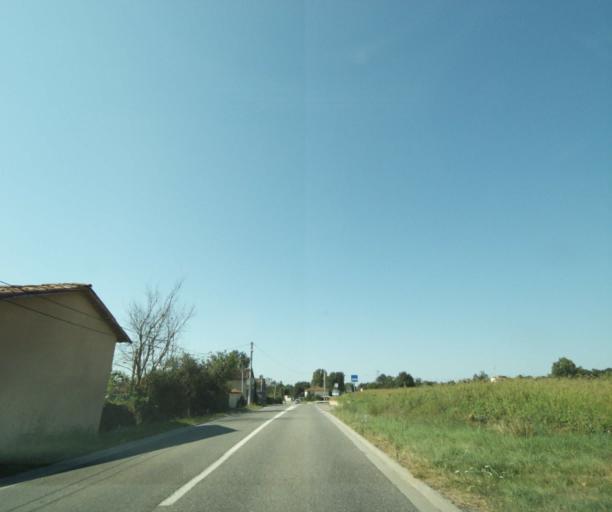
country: FR
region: Midi-Pyrenees
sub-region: Departement de la Haute-Garonne
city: Beaumont-sur-Leze
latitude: 43.3666
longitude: 1.3309
